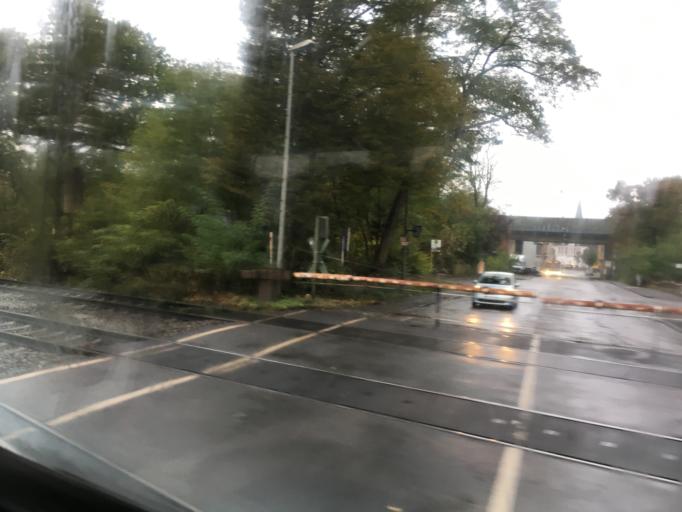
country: DE
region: North Rhine-Westphalia
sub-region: Regierungsbezirk Arnsberg
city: Herne
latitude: 51.5620
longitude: 7.1955
